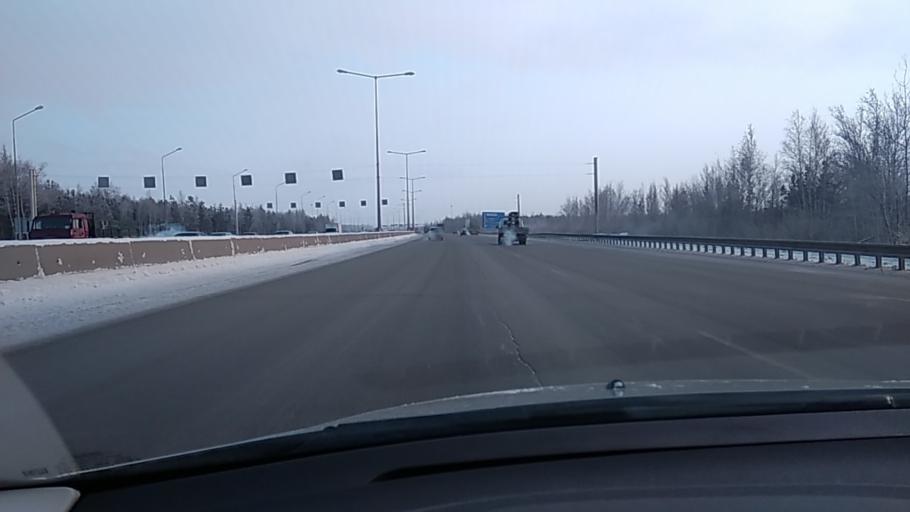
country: RU
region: Sverdlovsk
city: Istok
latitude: 56.7637
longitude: 60.7511
